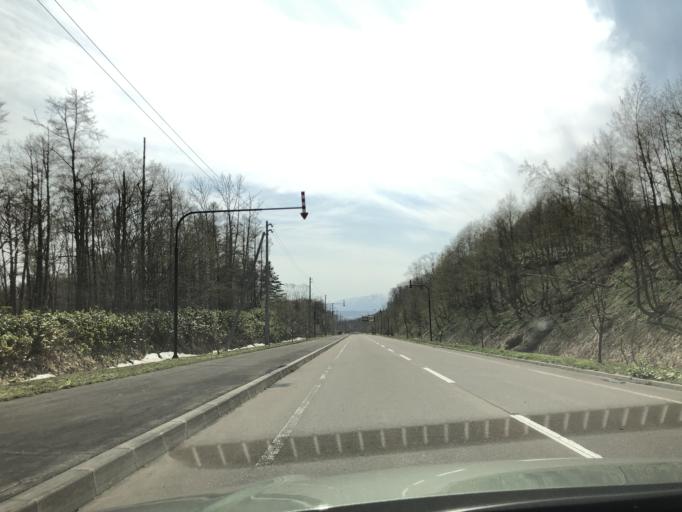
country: JP
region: Hokkaido
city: Akabira
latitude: 43.5941
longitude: 142.0419
